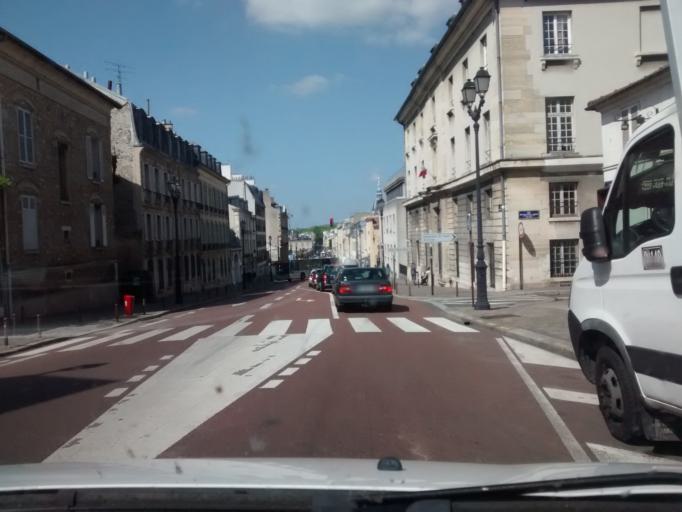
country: FR
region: Ile-de-France
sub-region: Departement des Yvelines
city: Versailles
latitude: 48.7941
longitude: 2.1207
